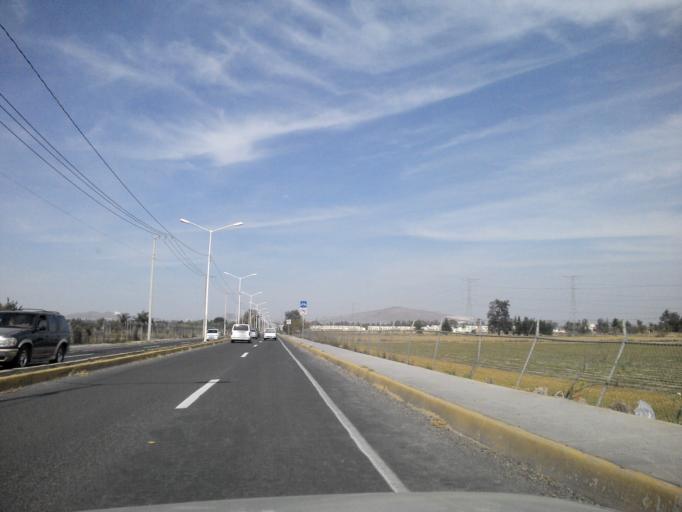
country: MX
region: Jalisco
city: San Sebastian el Grande
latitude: 20.5207
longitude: -103.4096
